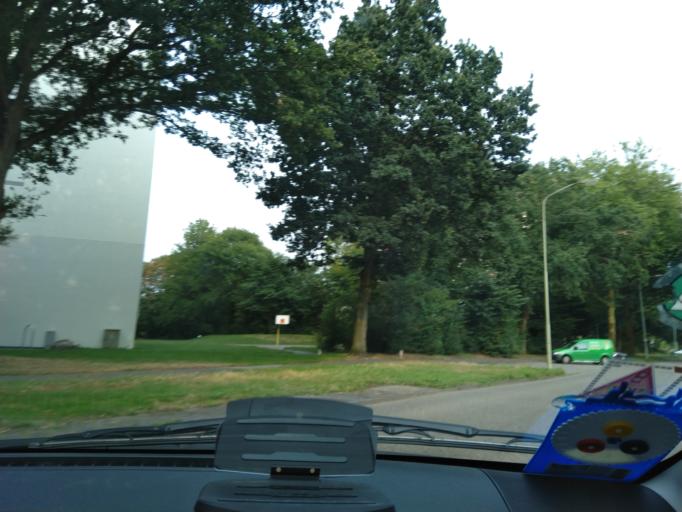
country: NL
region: Drenthe
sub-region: Gemeente Assen
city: Assen
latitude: 53.0107
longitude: 6.5643
